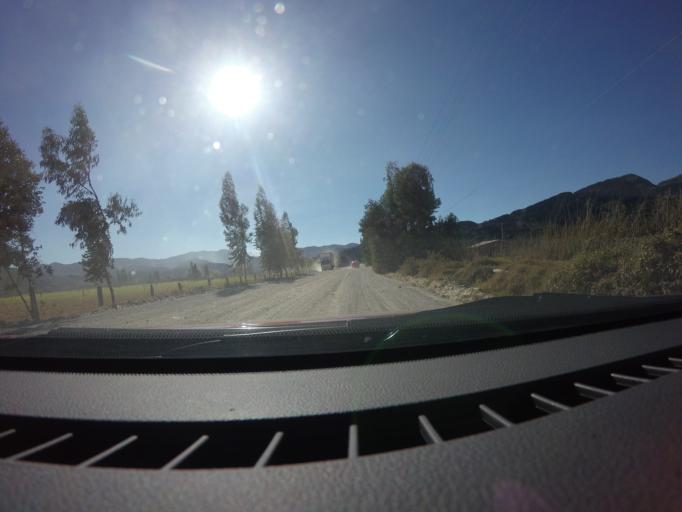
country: CO
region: Cundinamarca
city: Cucunuba
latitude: 5.2709
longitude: -73.7975
